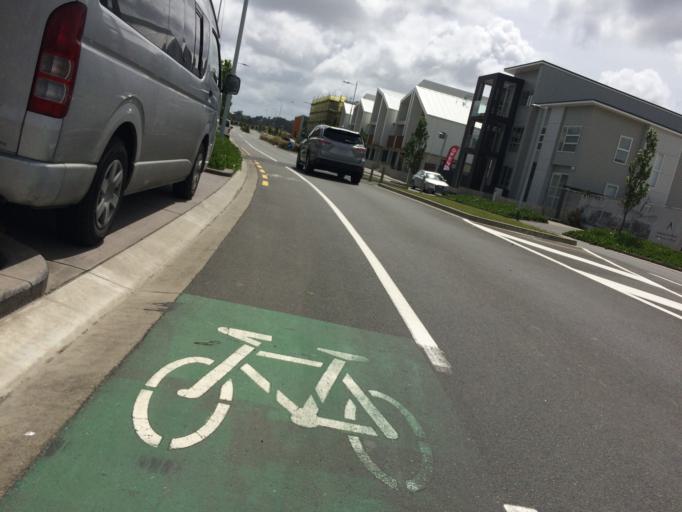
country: NZ
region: Auckland
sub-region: Auckland
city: Rosebank
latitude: -36.7938
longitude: 174.6598
